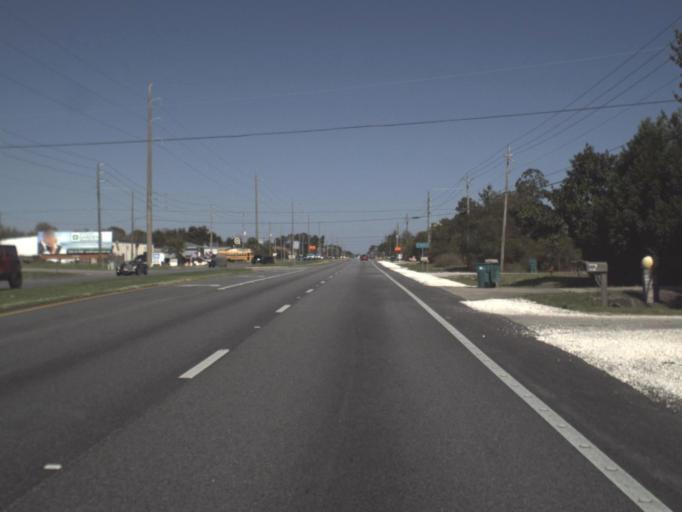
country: US
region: Florida
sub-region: Santa Rosa County
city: Navarre
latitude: 30.4108
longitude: -86.7666
